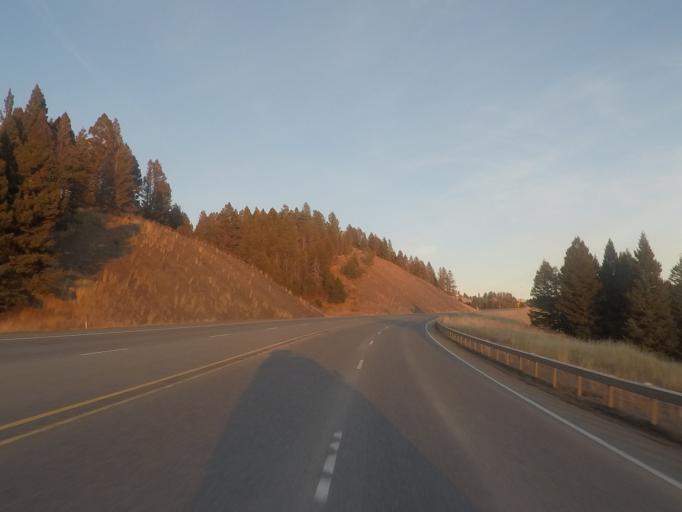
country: US
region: Montana
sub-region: Lewis and Clark County
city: Helena West Side
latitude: 46.5594
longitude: -112.3473
